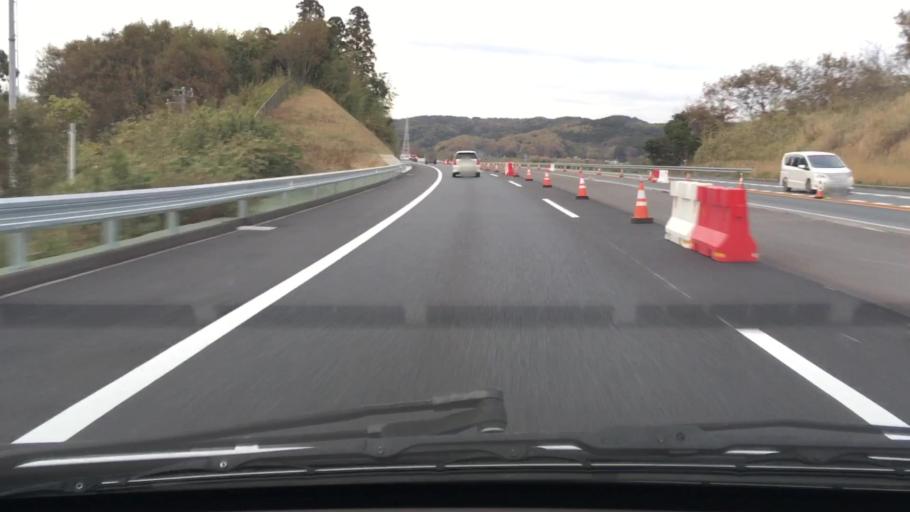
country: JP
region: Chiba
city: Kimitsu
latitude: 35.3025
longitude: 139.9405
